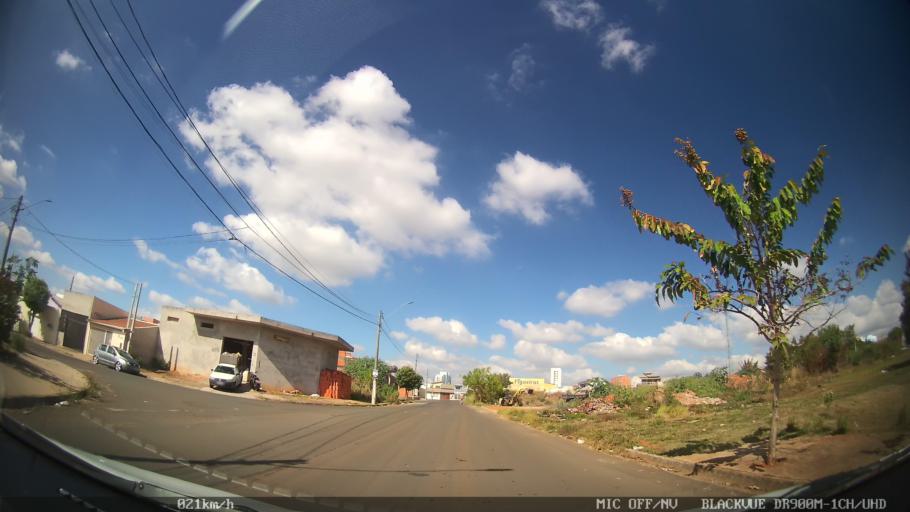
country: BR
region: Sao Paulo
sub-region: Hortolandia
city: Hortolandia
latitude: -22.8842
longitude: -47.2214
